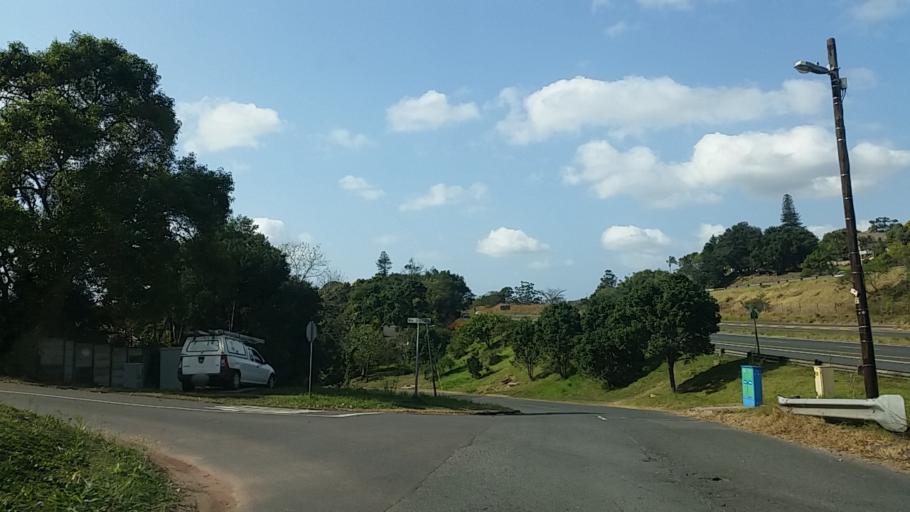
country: ZA
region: KwaZulu-Natal
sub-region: eThekwini Metropolitan Municipality
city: Berea
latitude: -29.8357
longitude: 30.9035
